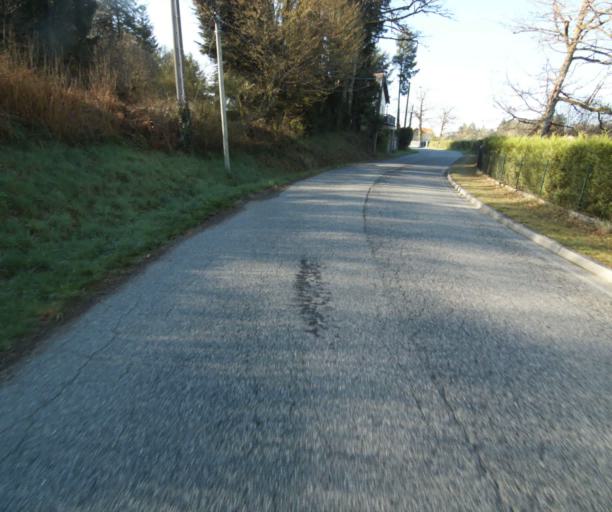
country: FR
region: Limousin
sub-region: Departement de la Correze
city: Correze
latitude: 45.3266
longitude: 1.8777
